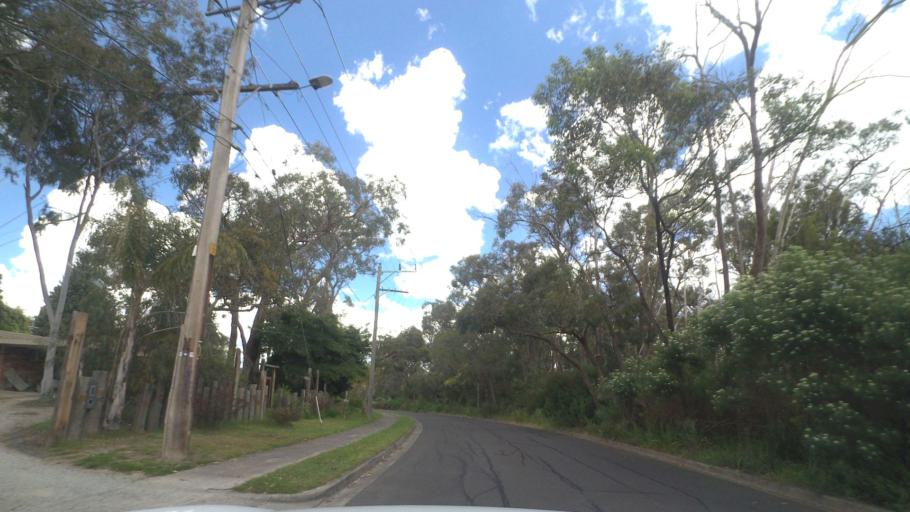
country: AU
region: Victoria
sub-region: Maroondah
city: Croydon South
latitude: -37.8087
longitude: 145.2627
